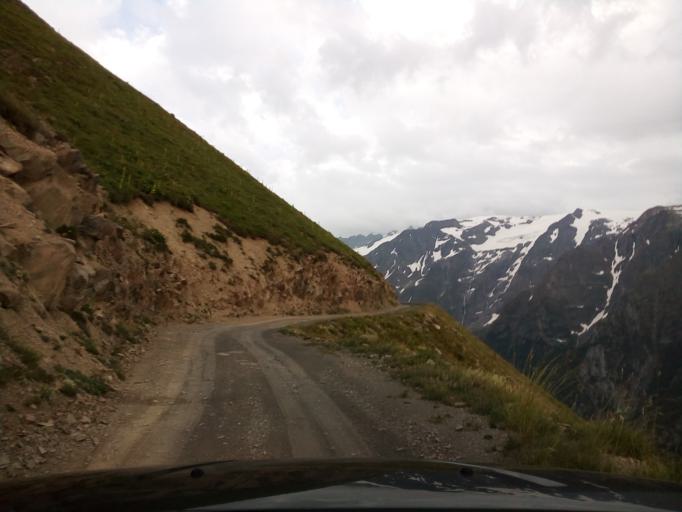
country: FR
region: Rhone-Alpes
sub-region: Departement de l'Isere
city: Mont-de-Lans
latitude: 45.0512
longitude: 6.1922
